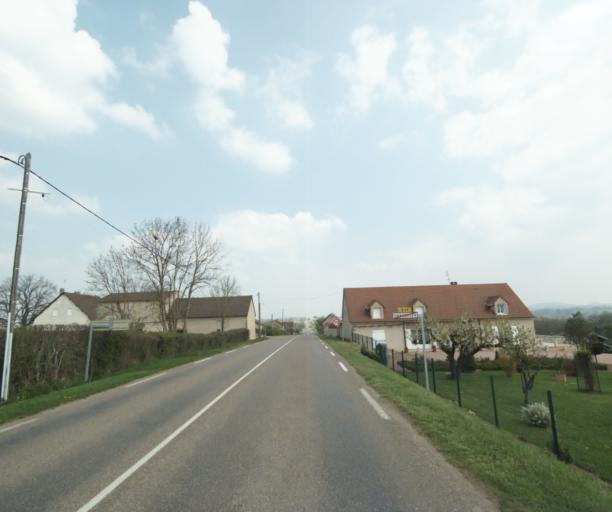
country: FR
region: Bourgogne
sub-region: Departement de Saone-et-Loire
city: Charolles
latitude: 46.4390
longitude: 4.2939
